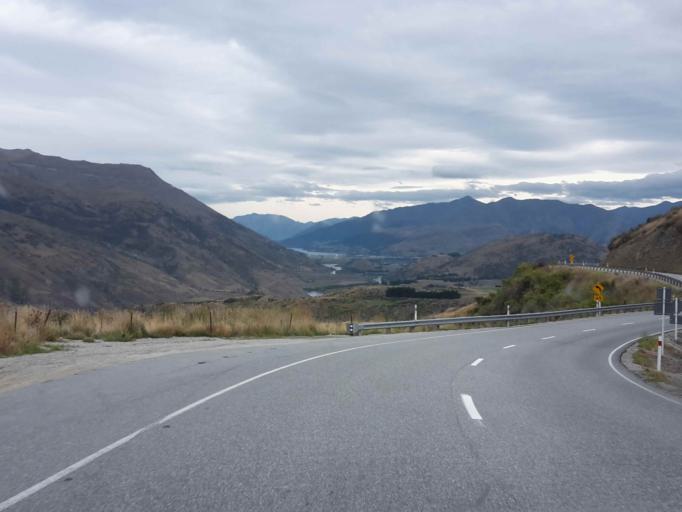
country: NZ
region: Otago
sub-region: Queenstown-Lakes District
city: Arrowtown
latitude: -44.9917
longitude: 168.9087
